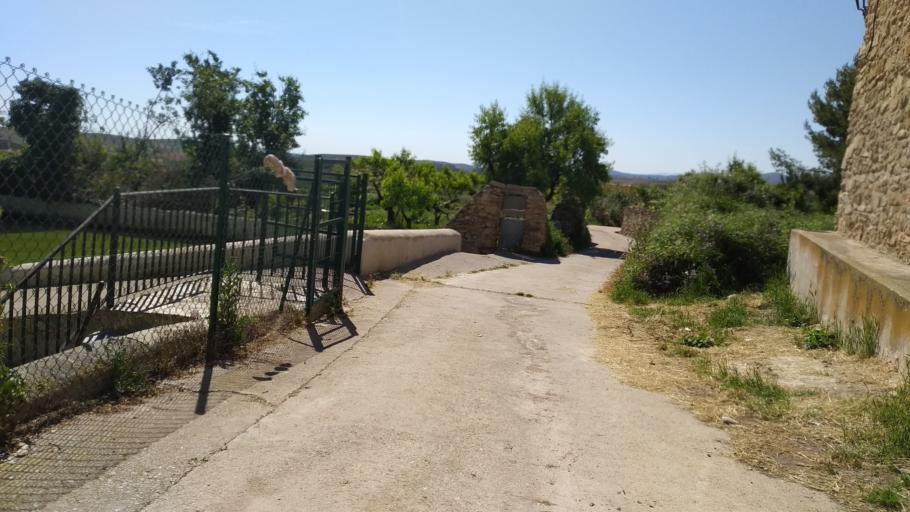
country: ES
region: Aragon
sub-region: Provincia de Teruel
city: Monforte de Moyuela
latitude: 41.0534
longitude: -1.0146
